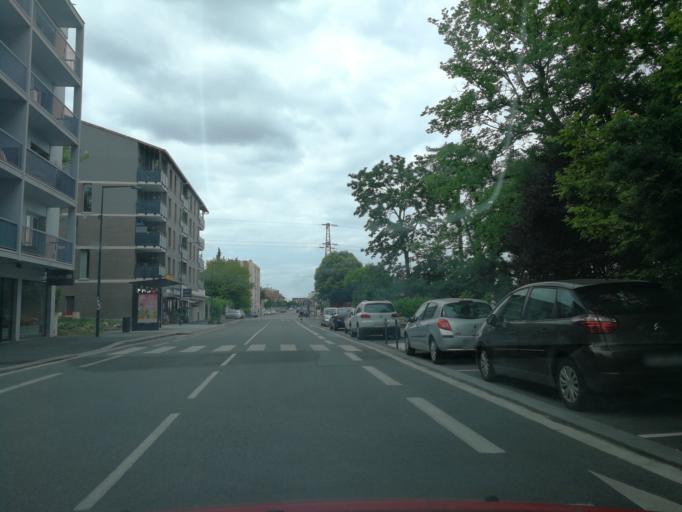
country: FR
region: Midi-Pyrenees
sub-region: Departement de la Haute-Garonne
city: Ramonville-Saint-Agne
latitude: 43.5493
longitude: 1.4712
